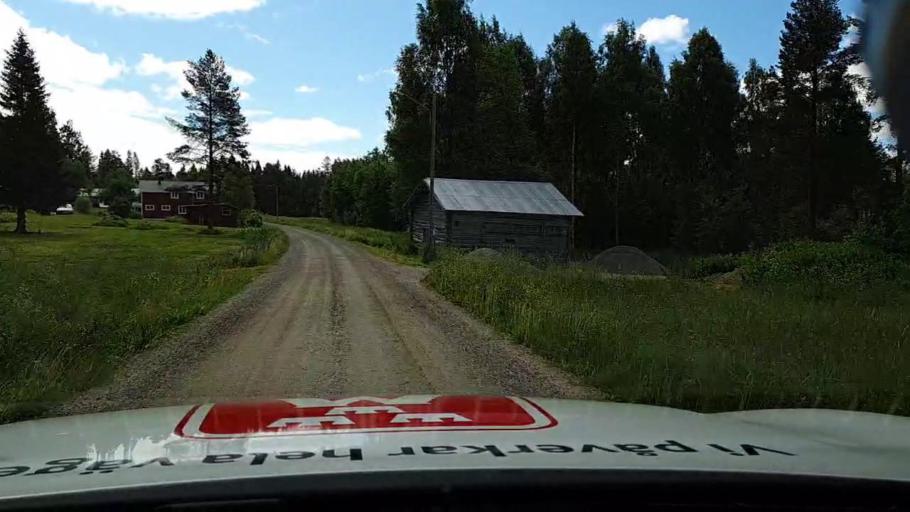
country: SE
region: Jaemtland
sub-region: Braecke Kommun
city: Braecke
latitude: 62.7605
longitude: 15.4995
